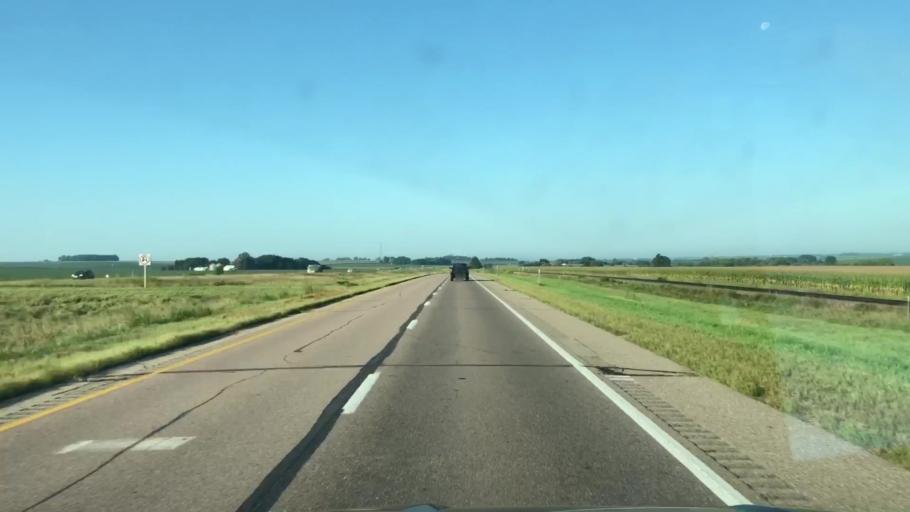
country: US
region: Iowa
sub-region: Sioux County
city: Alton
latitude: 43.0201
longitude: -95.9538
